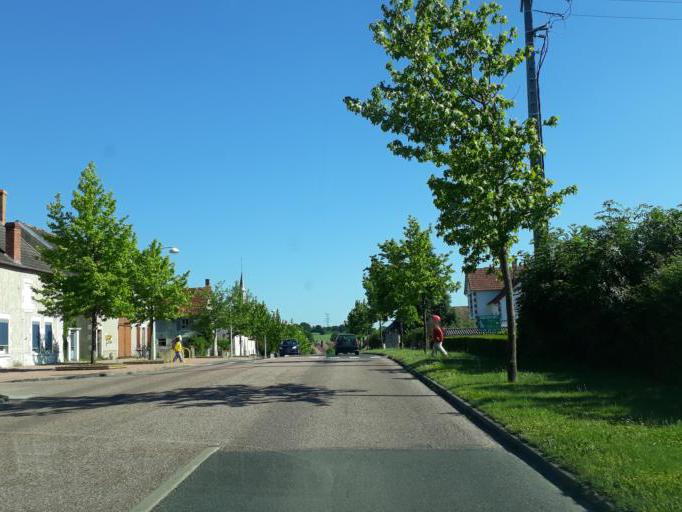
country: FR
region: Centre
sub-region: Departement du Cher
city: Lere
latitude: 47.4740
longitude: 2.9281
